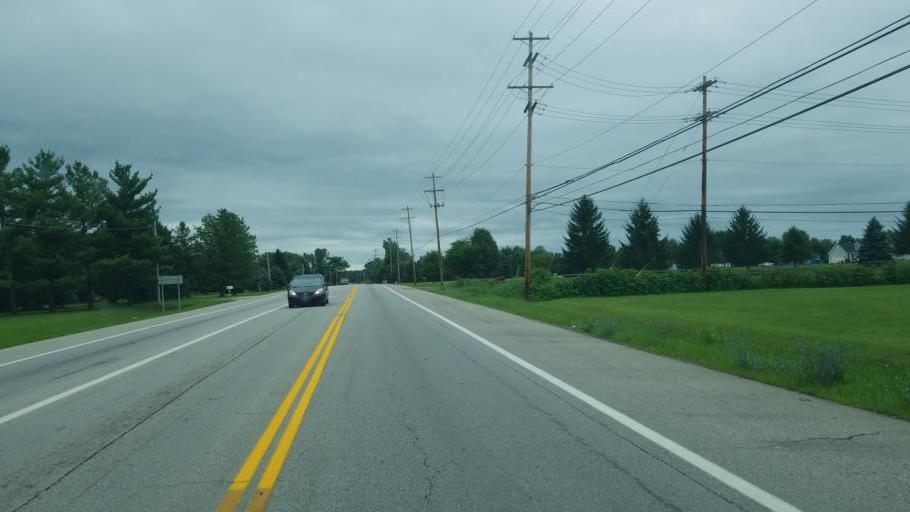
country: US
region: Ohio
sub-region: Pickaway County
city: Commercial Point
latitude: 39.8251
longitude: -83.0326
